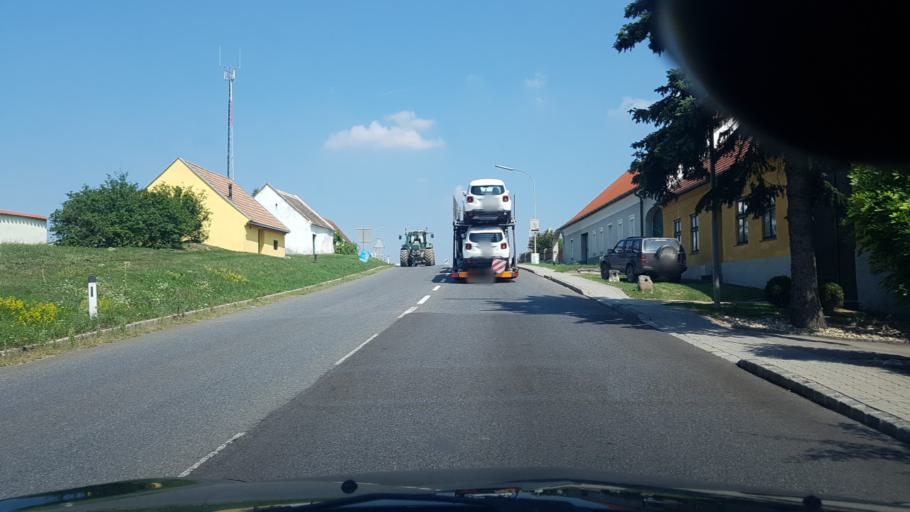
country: AT
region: Lower Austria
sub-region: Politischer Bezirk Mistelbach
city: Drasenhofen
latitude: 48.7589
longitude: 16.6474
